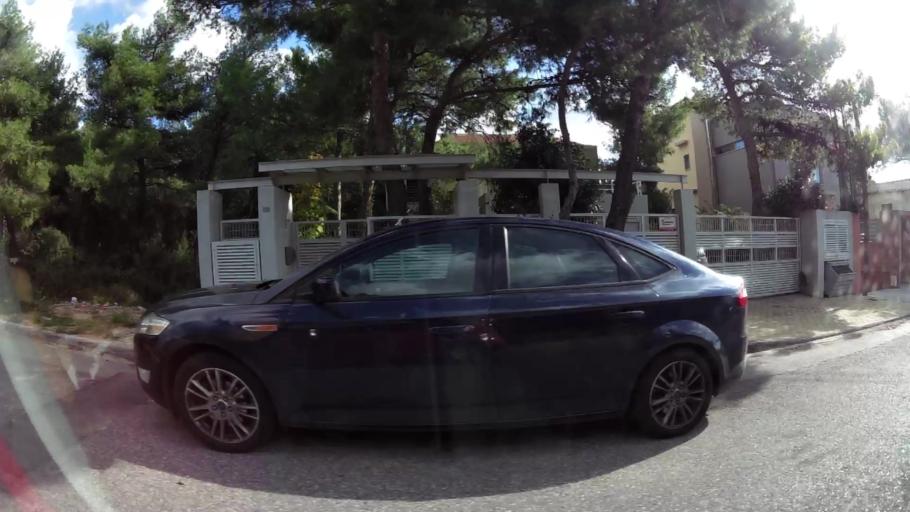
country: GR
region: Attica
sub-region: Nomarchia Anatolikis Attikis
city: Thrakomakedones
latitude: 38.1318
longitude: 23.7638
